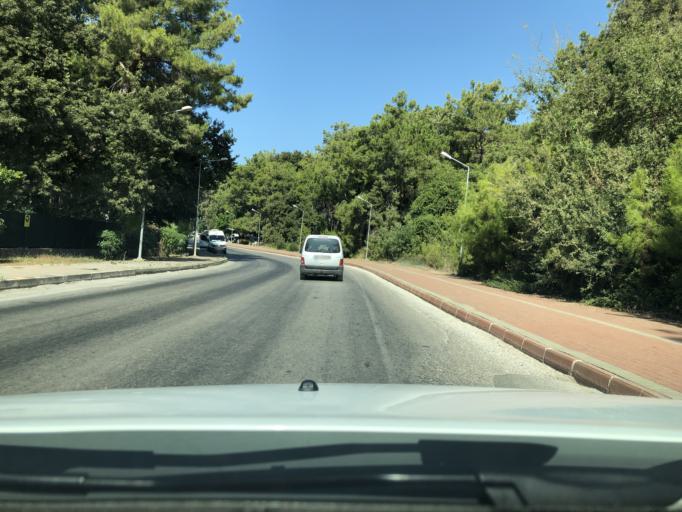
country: TR
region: Antalya
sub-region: Manavgat
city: Side
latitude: 36.7591
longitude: 31.4219
